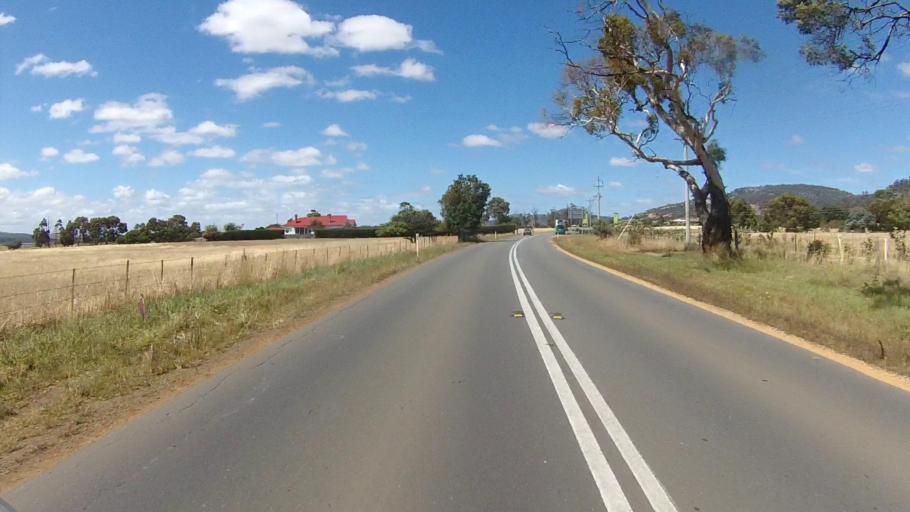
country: AU
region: Tasmania
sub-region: Clarence
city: Cambridge
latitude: -42.7748
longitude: 147.4161
